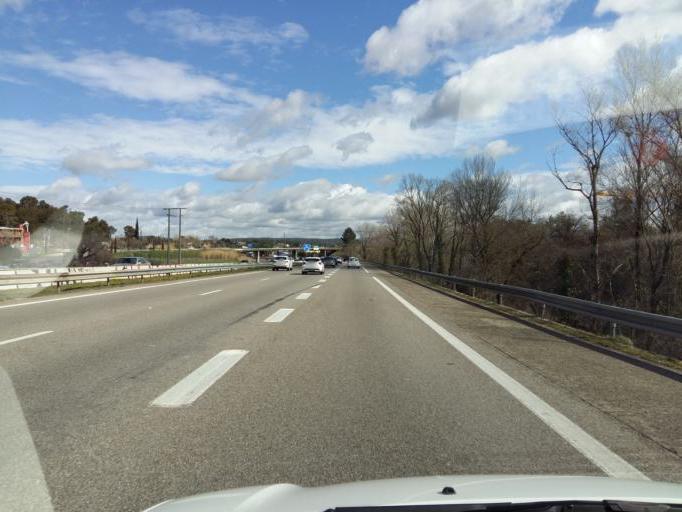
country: FR
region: Provence-Alpes-Cote d'Azur
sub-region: Departement des Bouches-du-Rhone
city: Aix-en-Provence
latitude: 43.5113
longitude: 5.4211
